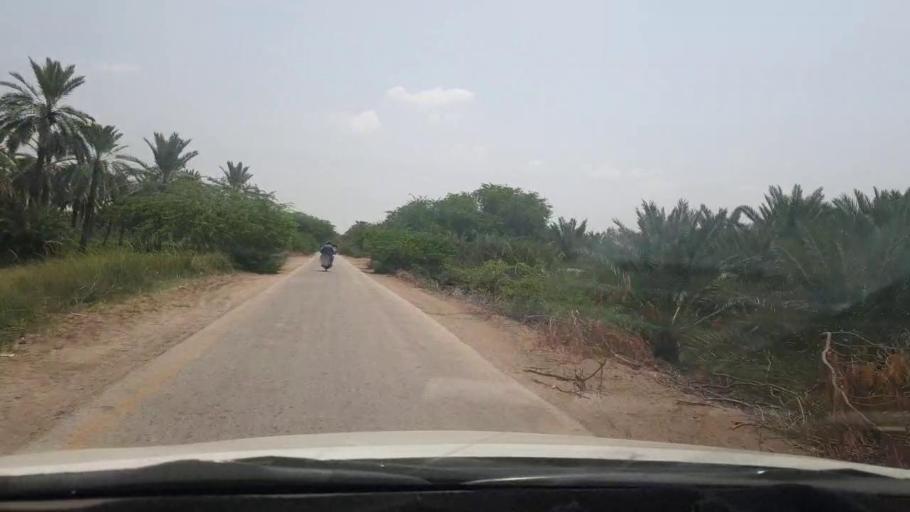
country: PK
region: Sindh
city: Khairpur
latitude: 27.5328
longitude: 68.8957
